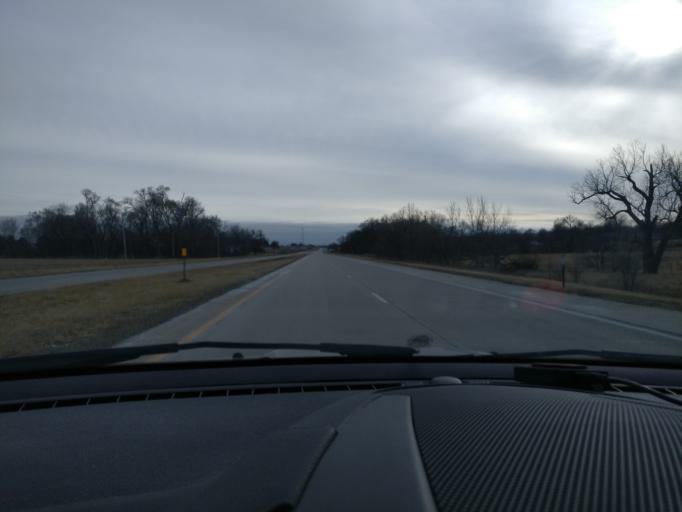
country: US
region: Nebraska
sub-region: Saunders County
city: Wahoo
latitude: 41.0665
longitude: -96.6404
